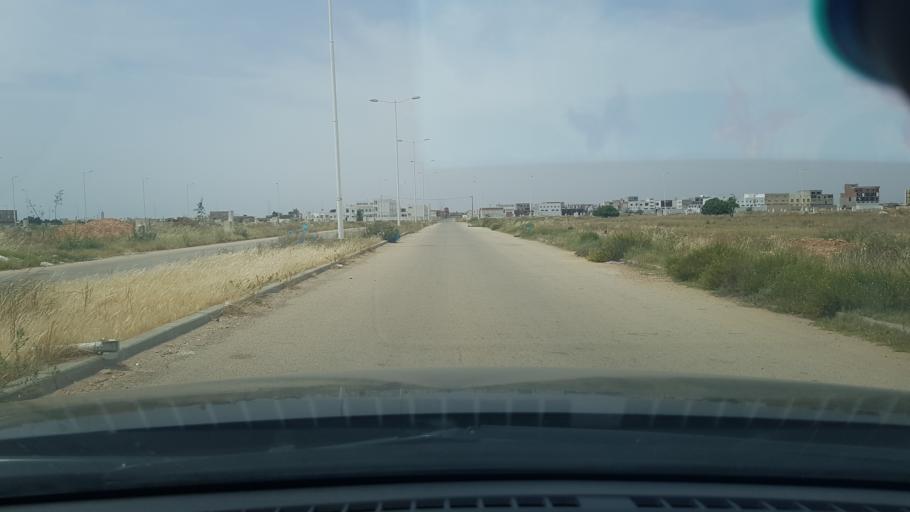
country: TN
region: Safaqis
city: Al Qarmadah
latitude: 34.8287
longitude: 10.7469
